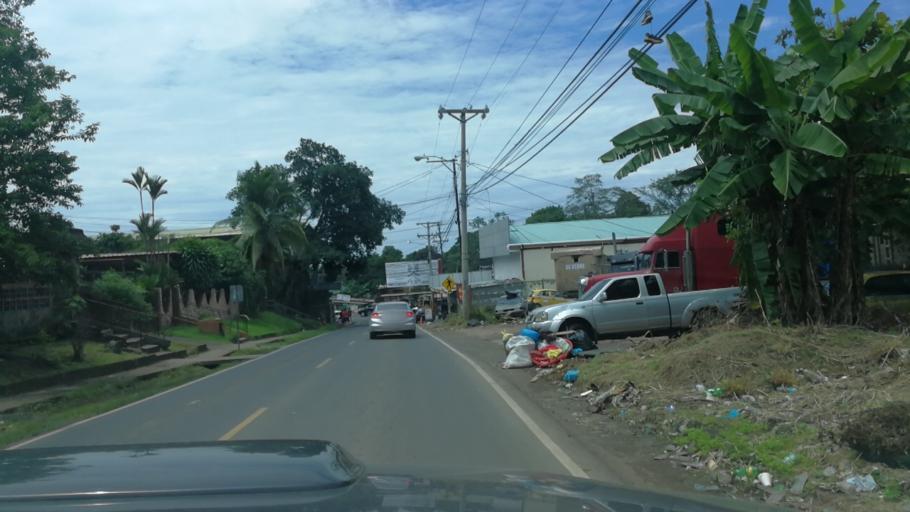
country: PA
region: Panama
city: Tocumen
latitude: 9.0722
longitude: -79.4269
